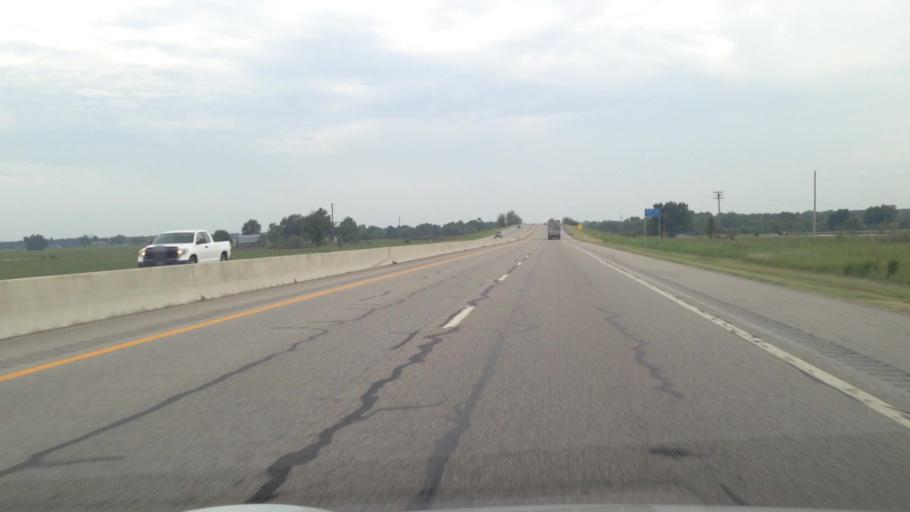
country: US
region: Oklahoma
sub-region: Ottawa County
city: Miami
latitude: 36.8202
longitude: -94.8714
